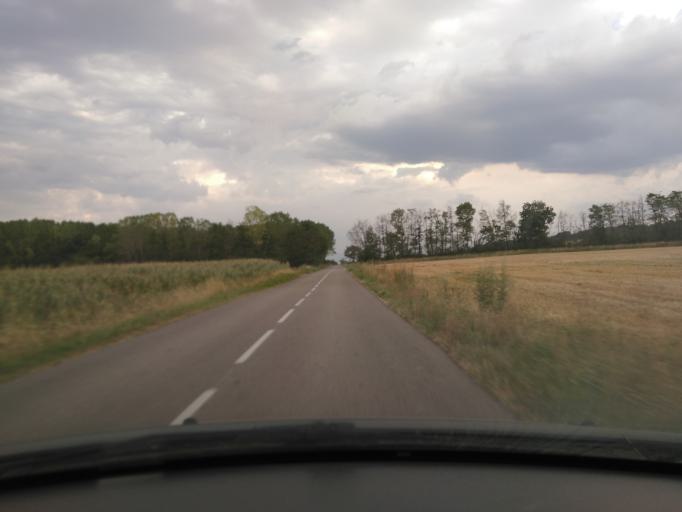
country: FR
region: Rhone-Alpes
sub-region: Departement de l'Isere
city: Beaurepaire
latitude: 45.3991
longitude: 5.0605
